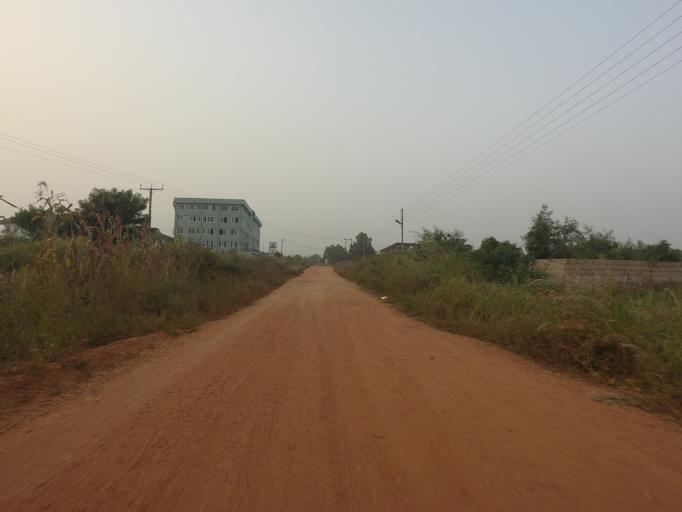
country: GH
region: Volta
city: Anloga
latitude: 5.9850
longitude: 0.6008
